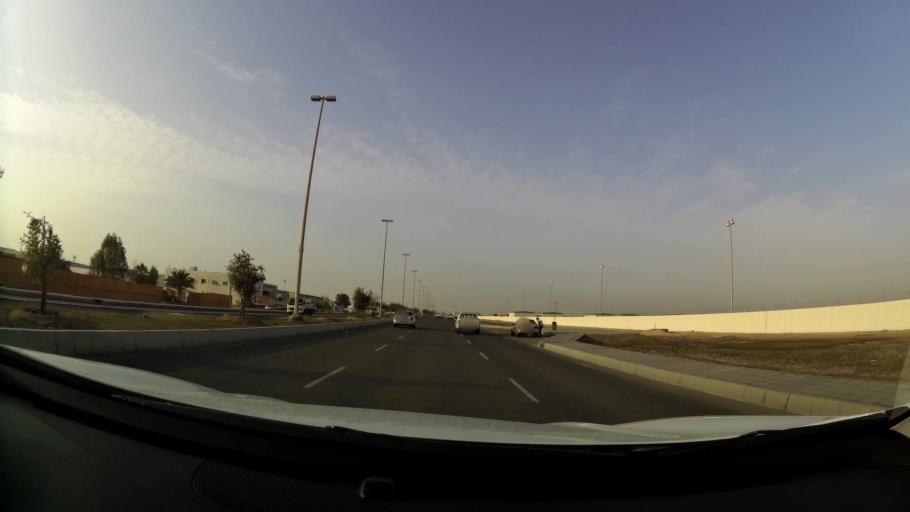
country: AE
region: Abu Dhabi
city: Abu Dhabi
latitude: 24.3475
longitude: 54.5025
